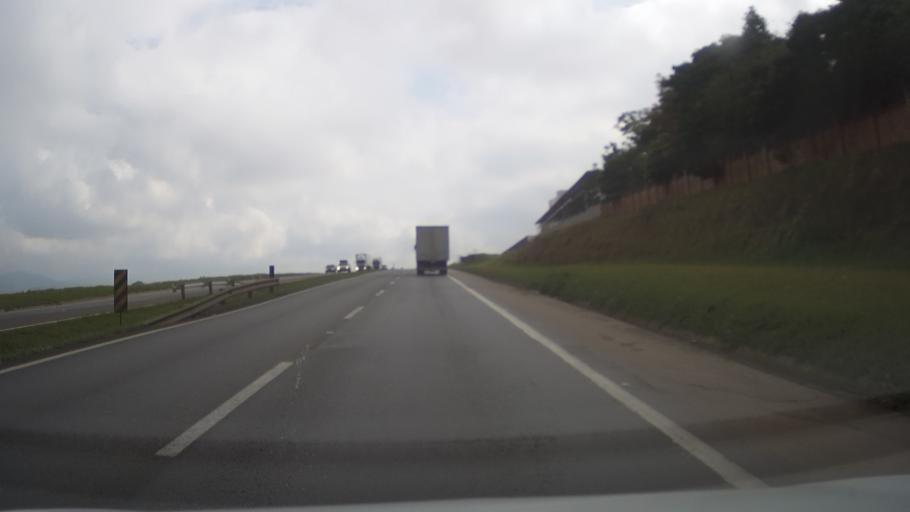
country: BR
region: Minas Gerais
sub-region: Extrema
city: Extrema
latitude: -22.8439
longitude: -46.3308
